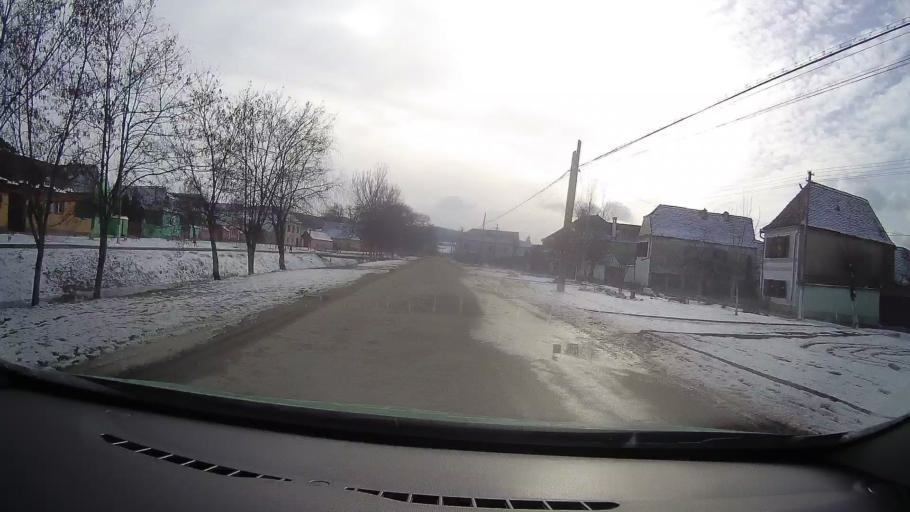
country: RO
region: Sibiu
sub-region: Comuna Bradeni
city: Bradeni
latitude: 46.0809
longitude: 24.8293
